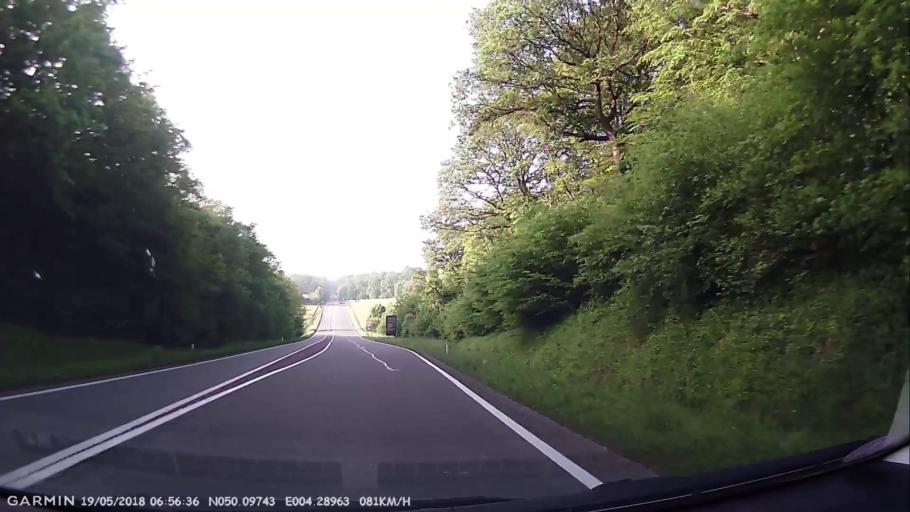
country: BE
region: Wallonia
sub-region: Province du Hainaut
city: Chimay
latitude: 50.0973
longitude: 4.2897
